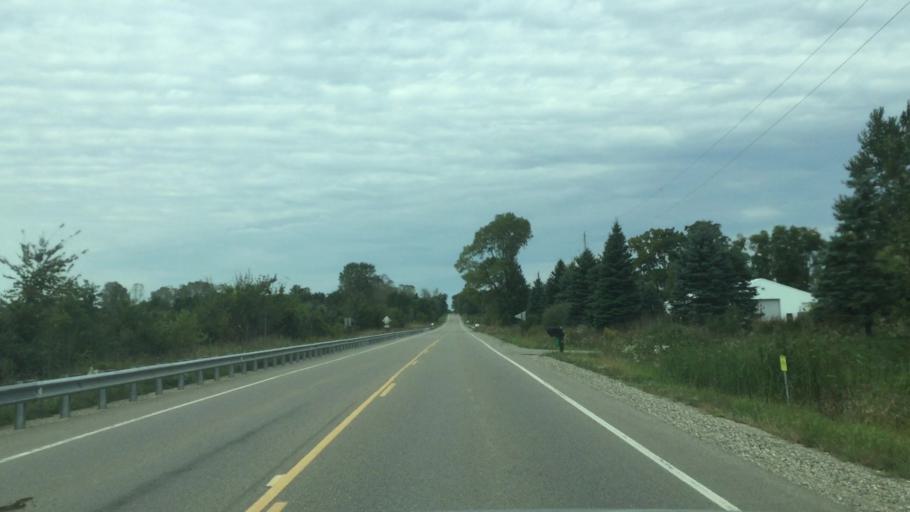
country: US
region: Michigan
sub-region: Livingston County
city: Howell
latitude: 42.6745
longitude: -83.8389
